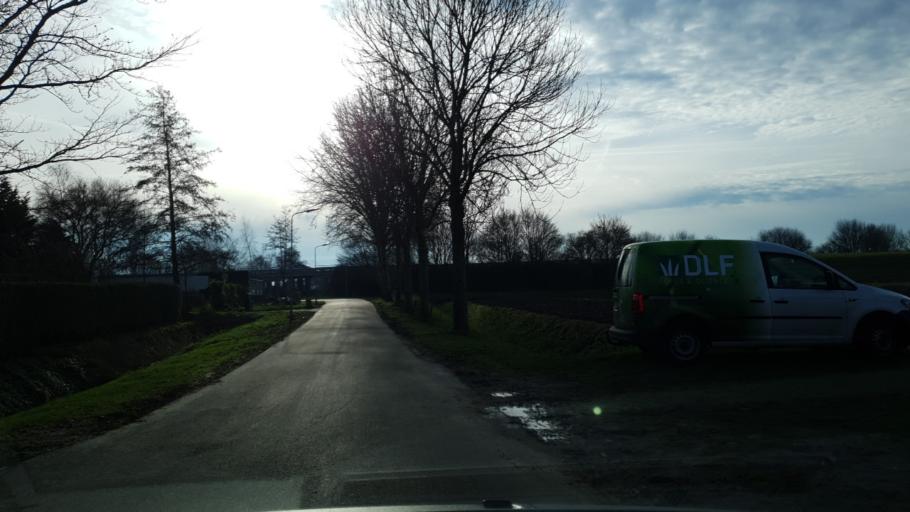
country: NL
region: Zeeland
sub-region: Gemeente Reimerswaal
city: Yerseke
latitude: 51.4216
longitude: 4.1049
